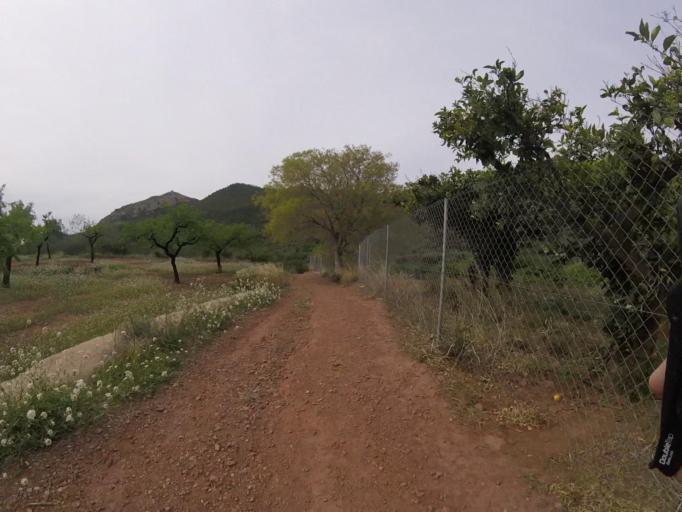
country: ES
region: Valencia
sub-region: Provincia de Castello
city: Benicassim
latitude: 40.0746
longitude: 0.0361
